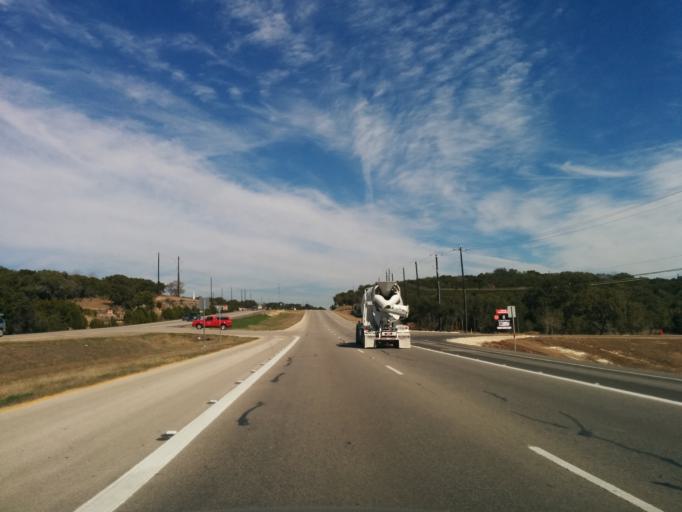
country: US
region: Texas
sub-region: Comal County
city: Bulverde
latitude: 29.7700
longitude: -98.4276
